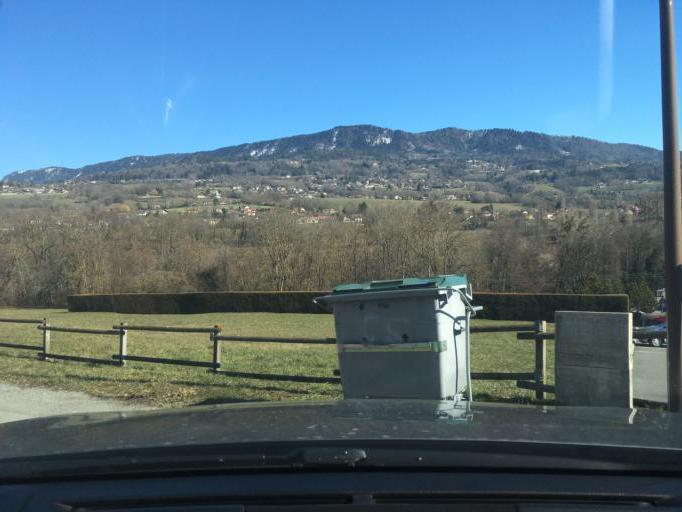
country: FR
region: Rhone-Alpes
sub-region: Departement de la Haute-Savoie
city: Cranves-Sales
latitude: 46.1856
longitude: 6.2928
